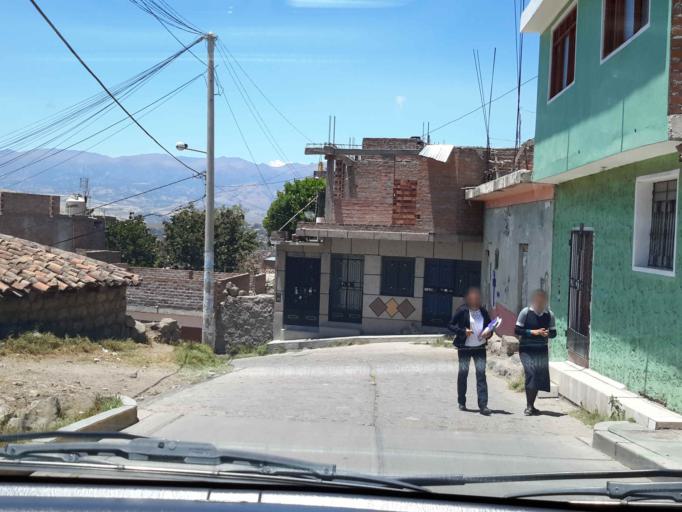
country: PE
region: Ayacucho
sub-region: Provincia de Huamanga
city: Ayacucho
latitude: -13.1687
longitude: -74.2229
